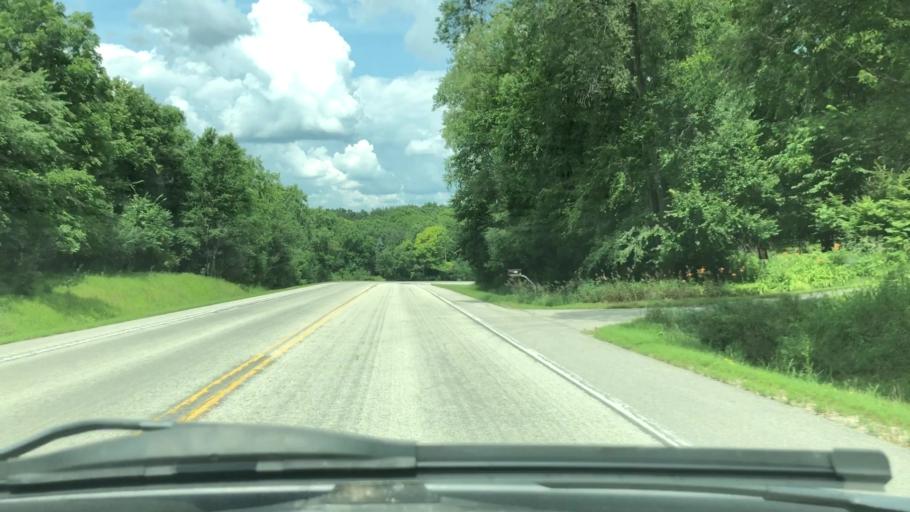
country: US
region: Minnesota
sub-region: Olmsted County
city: Rochester
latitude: 43.9694
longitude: -92.5183
